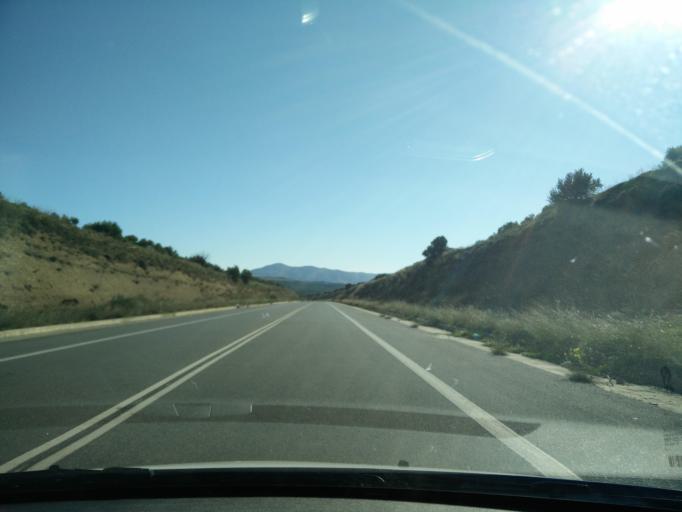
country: GR
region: Crete
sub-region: Nomos Irakleiou
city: Arkalochori
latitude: 35.1128
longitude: 25.2900
